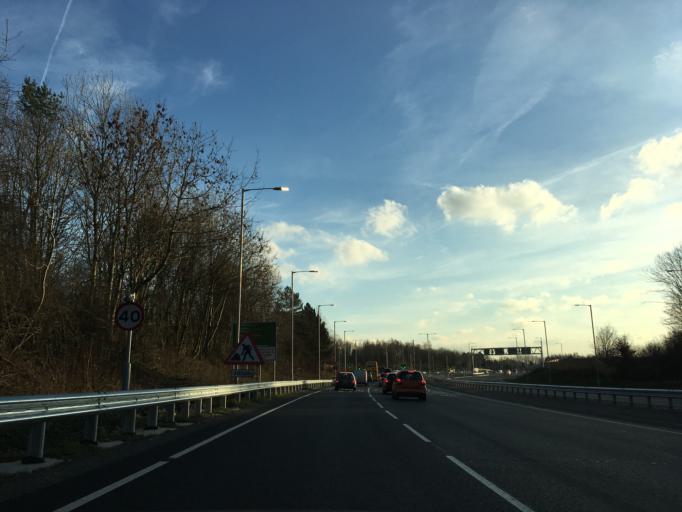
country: GB
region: England
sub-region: Borough of Stockport
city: Cheadle Hulme
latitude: 53.3610
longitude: -2.2001
